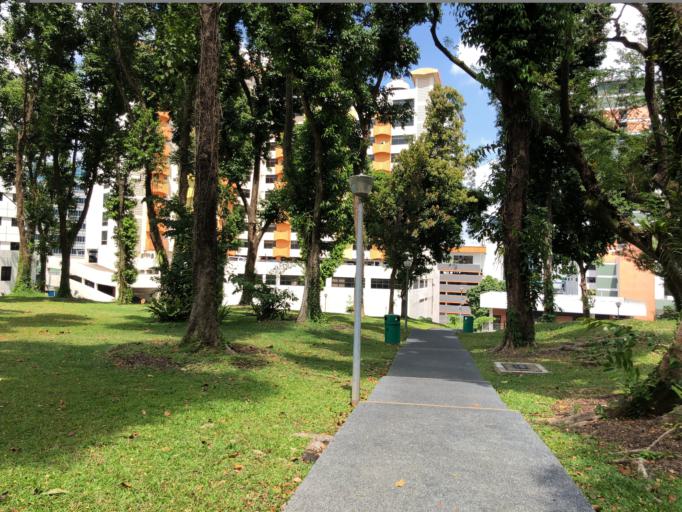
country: SG
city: Singapore
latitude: 1.2860
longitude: 103.8406
